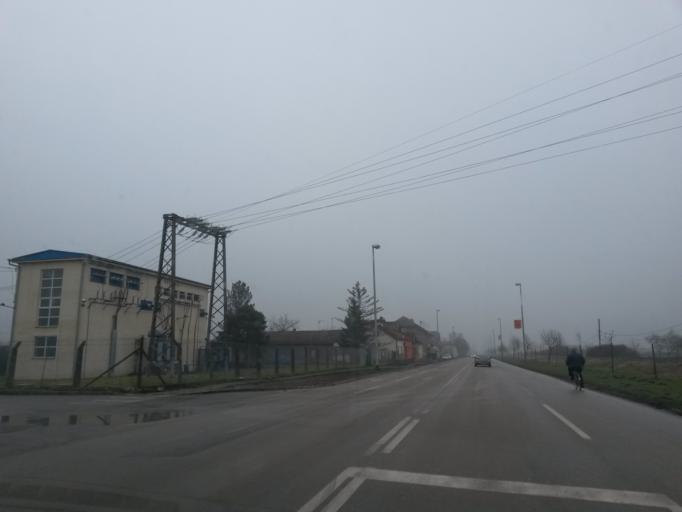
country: HR
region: Vukovarsko-Srijemska
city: Zupanja
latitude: 45.0902
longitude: 18.6969
